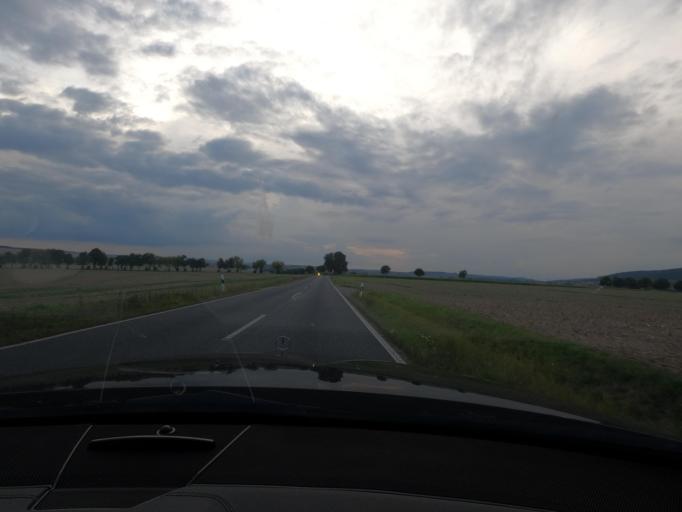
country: DE
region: Thuringia
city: Breitenworbis
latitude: 51.4000
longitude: 10.4271
